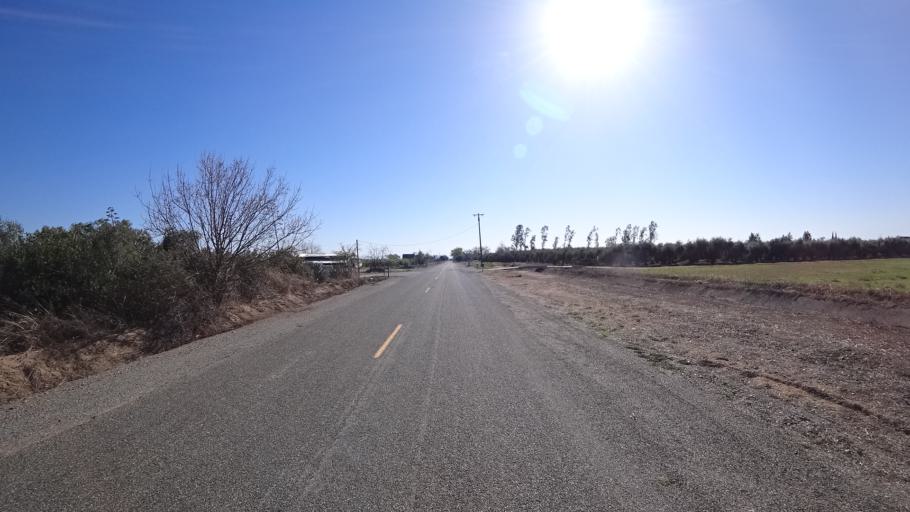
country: US
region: California
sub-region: Glenn County
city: Orland
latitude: 39.7476
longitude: -122.2268
